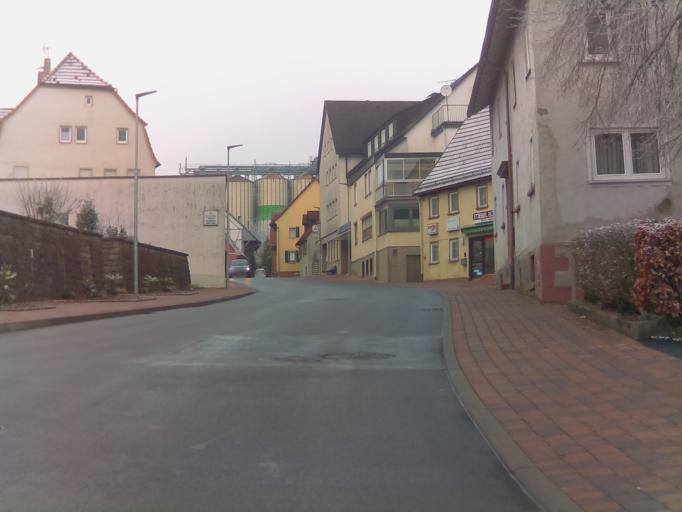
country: DE
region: Baden-Wuerttemberg
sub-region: Karlsruhe Region
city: Rosenberg
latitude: 49.4564
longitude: 9.4749
